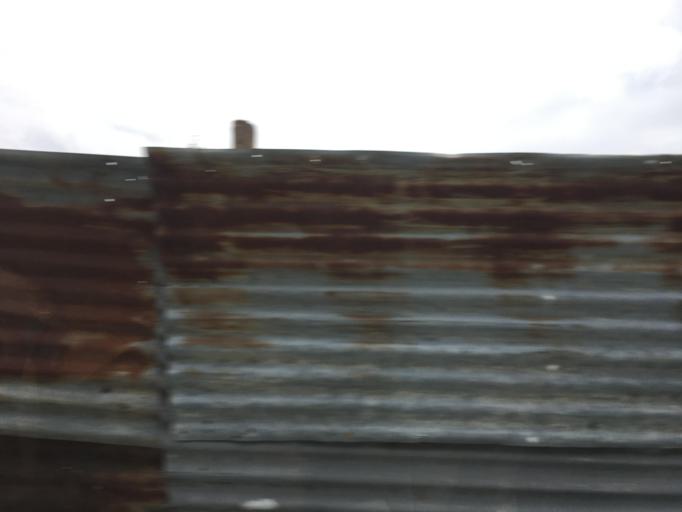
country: GT
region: Guatemala
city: Villa Canales
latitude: 14.4399
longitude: -90.5584
